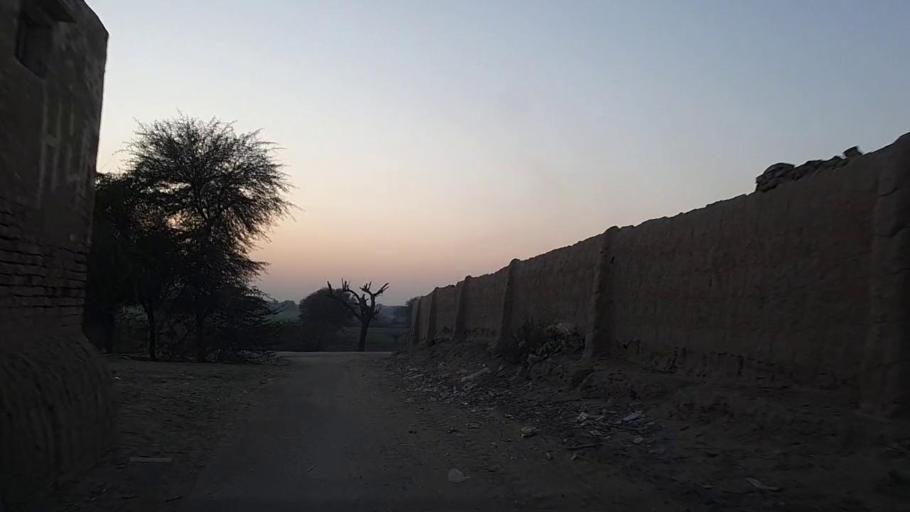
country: PK
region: Sindh
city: Daur
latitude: 26.4859
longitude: 68.4912
